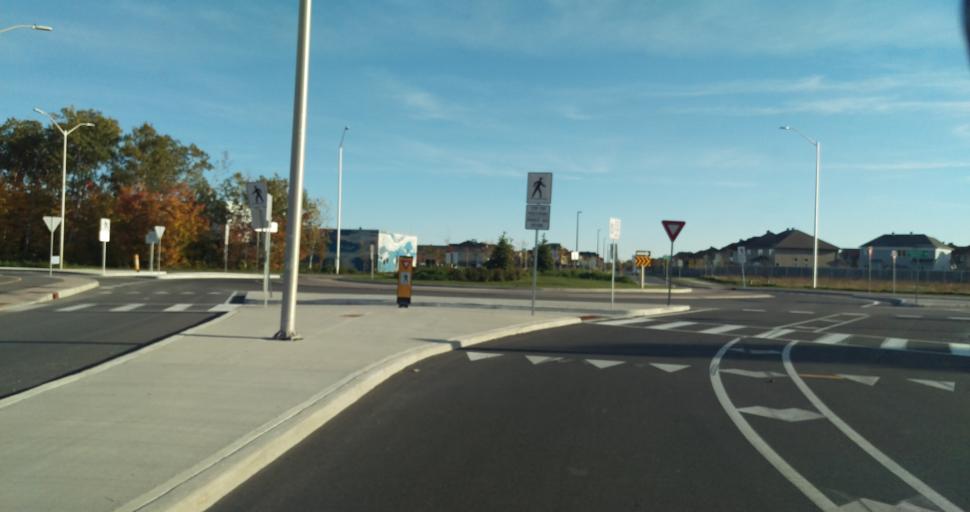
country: CA
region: Ontario
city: Clarence-Rockland
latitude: 45.4551
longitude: -75.4652
